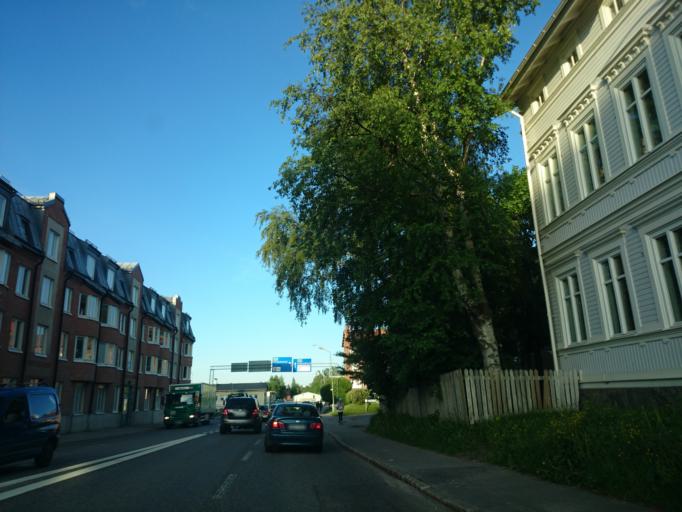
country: SE
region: Vaesternorrland
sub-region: Sundsvalls Kommun
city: Sundsvall
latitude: 62.3856
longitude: 17.3092
